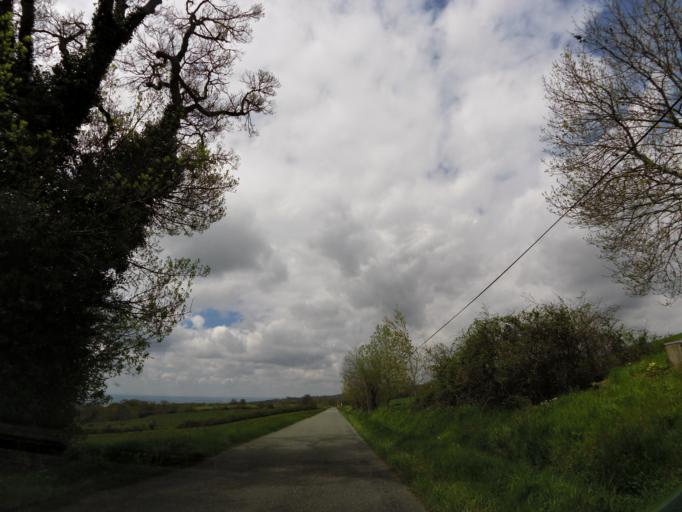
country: FR
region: Languedoc-Roussillon
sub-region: Departement de l'Aude
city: Villepinte
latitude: 43.3574
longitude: 2.1561
